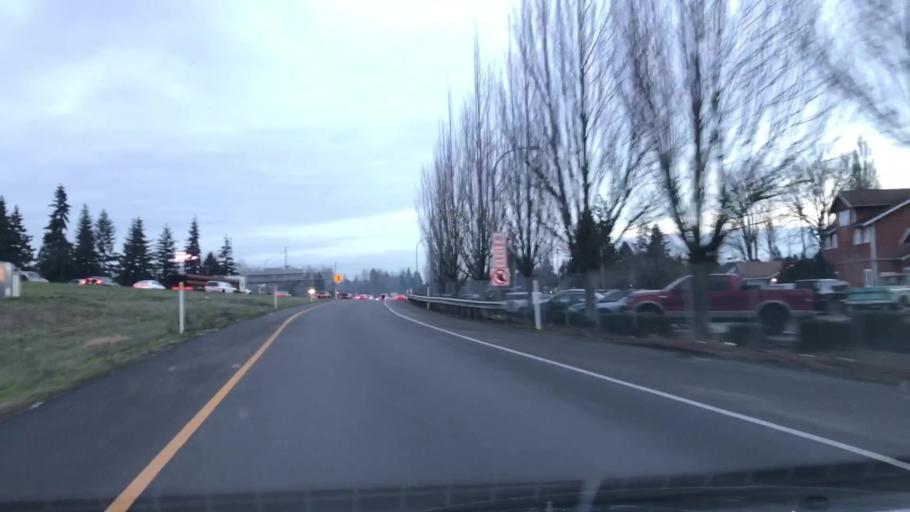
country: US
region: Washington
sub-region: Snohomish County
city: Marysville
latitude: 48.0528
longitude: -122.1839
